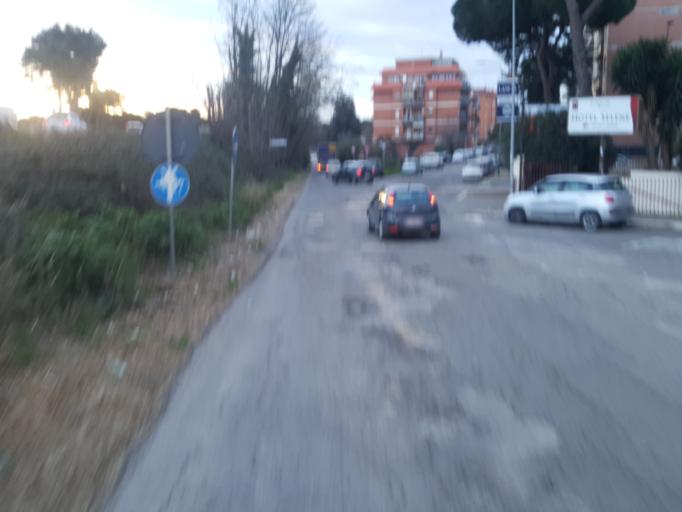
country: IT
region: Latium
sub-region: Citta metropolitana di Roma Capitale
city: Area Produttiva
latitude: 41.6747
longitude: 12.5017
